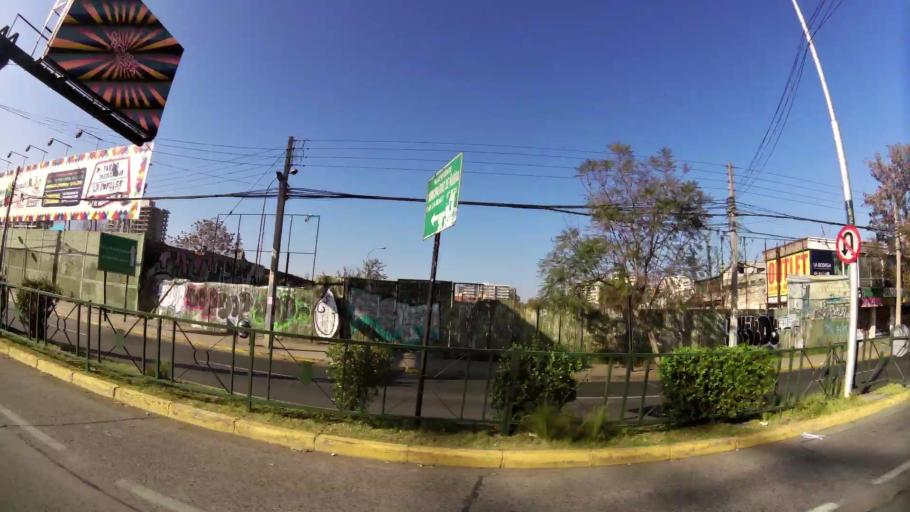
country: CL
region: Santiago Metropolitan
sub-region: Provincia de Santiago
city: Villa Presidente Frei, Nunoa, Santiago, Chile
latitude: -33.4544
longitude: -70.5720
